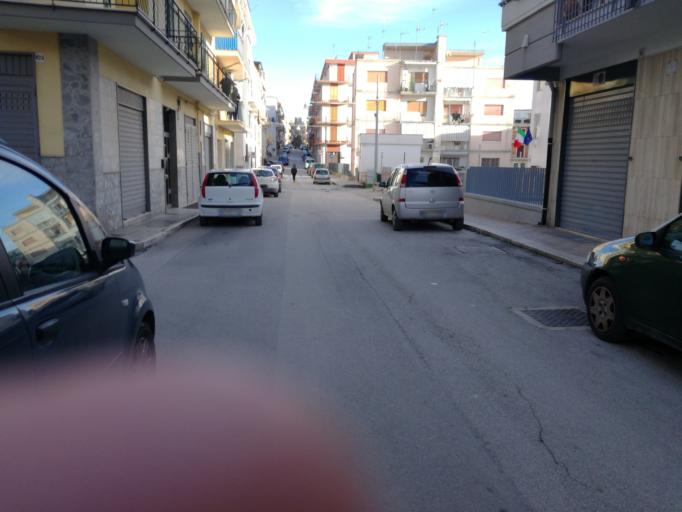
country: IT
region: Apulia
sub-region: Provincia di Bari
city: Ruvo di Puglia
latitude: 41.1154
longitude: 16.4806
